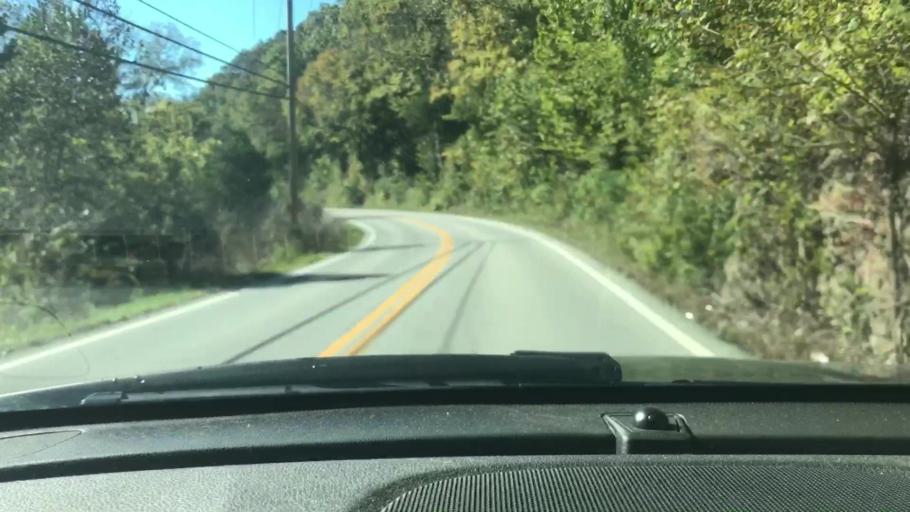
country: US
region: Tennessee
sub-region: Dickson County
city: Charlotte
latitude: 36.1818
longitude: -87.3151
